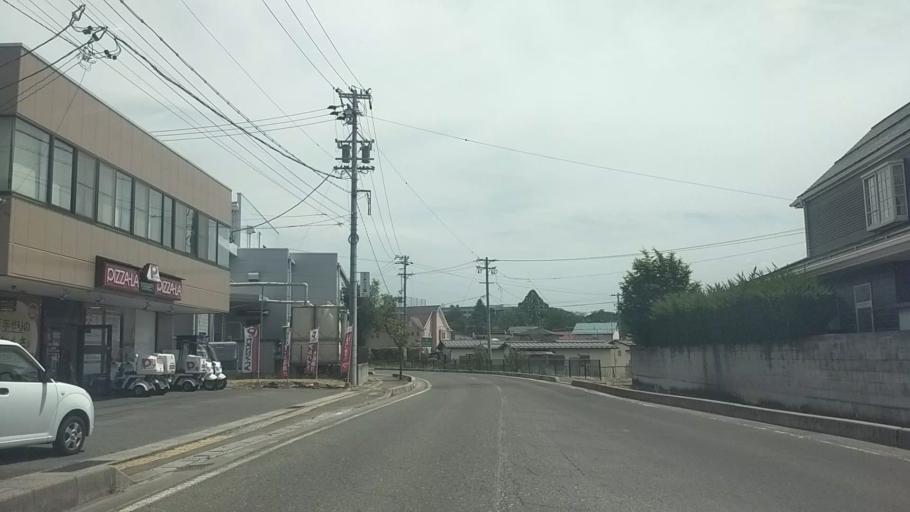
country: JP
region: Nagano
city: Chino
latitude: 35.9990
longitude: 138.1687
